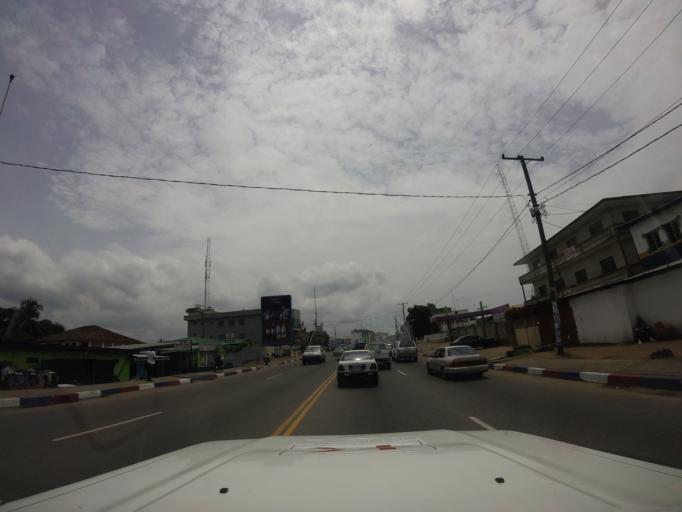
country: LR
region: Montserrado
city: Monrovia
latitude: 6.2942
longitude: -10.7859
